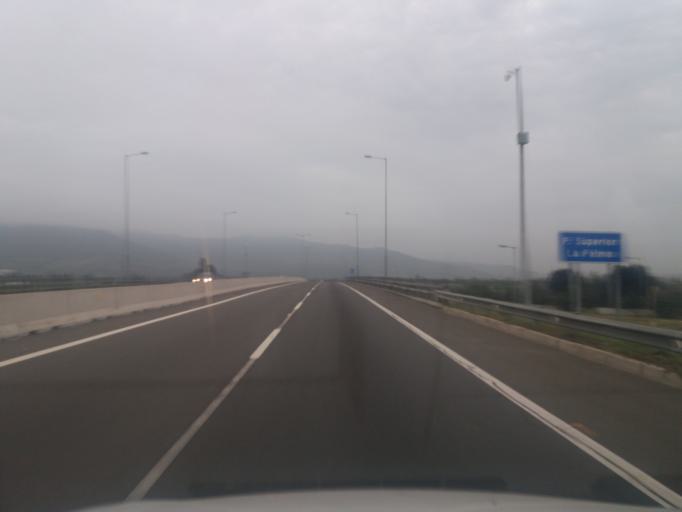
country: CL
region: Valparaiso
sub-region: Provincia de Quillota
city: Quillota
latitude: -32.8764
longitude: -71.2314
